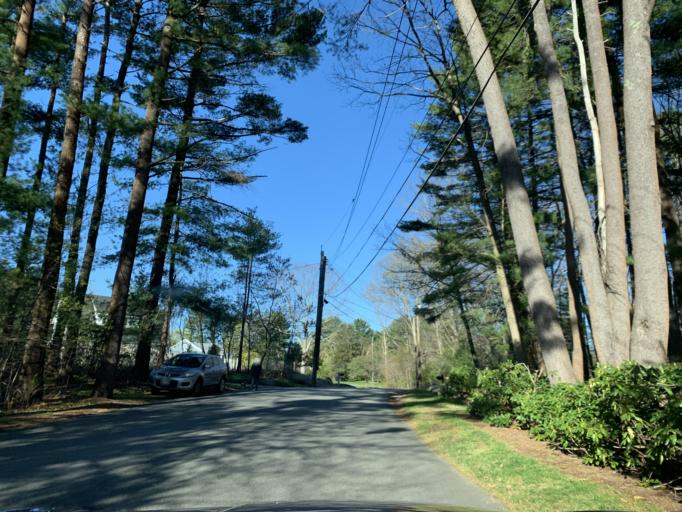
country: US
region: Massachusetts
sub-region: Norfolk County
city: Westwood
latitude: 42.2335
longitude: -71.2068
